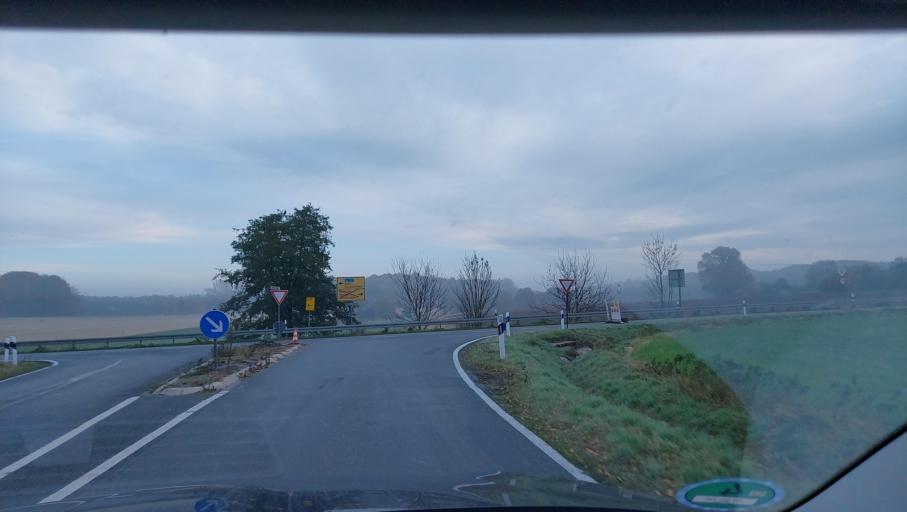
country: DE
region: Lower Saxony
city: Neuenkirchen
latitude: 52.1258
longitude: 8.3953
